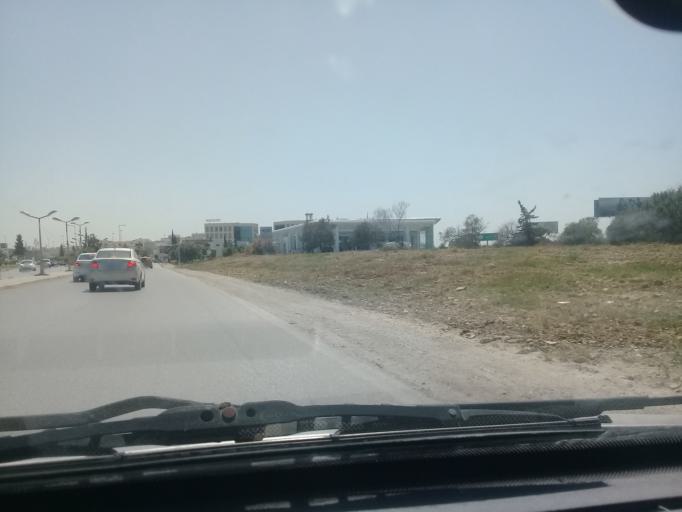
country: TN
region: Ariana
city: Ariana
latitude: 36.8424
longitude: 10.2496
